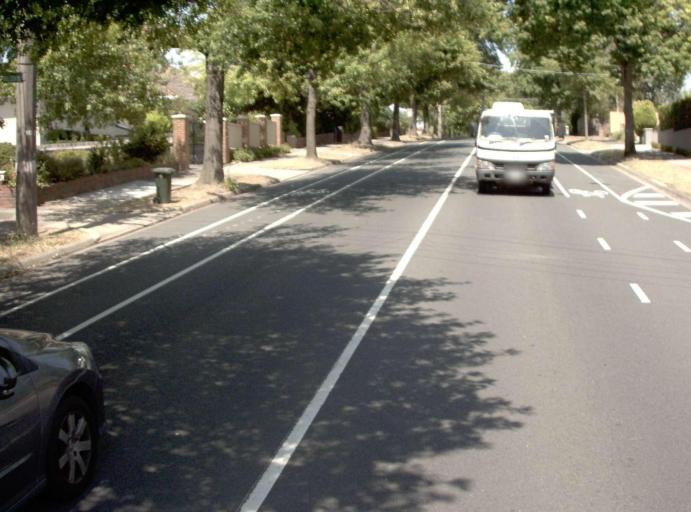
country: AU
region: Victoria
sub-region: Boroondara
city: Kew East
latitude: -37.7898
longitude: 145.0730
